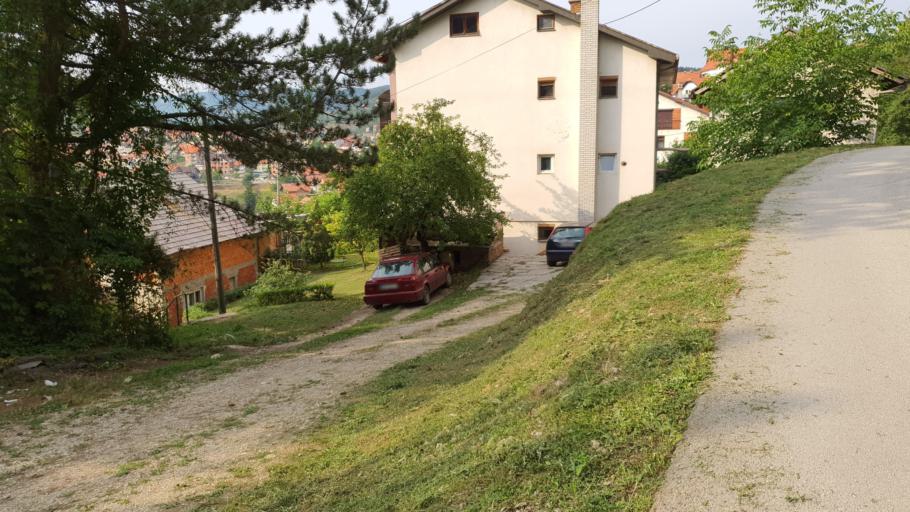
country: RS
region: Central Serbia
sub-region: Zlatiborski Okrug
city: Uzice
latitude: 43.8551
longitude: 19.8246
